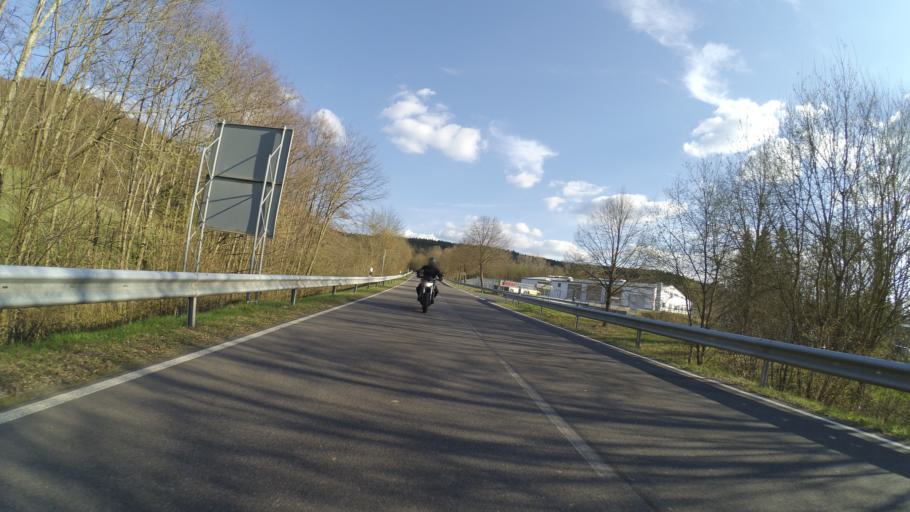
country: DE
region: Rheinland-Pfalz
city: Mullenbach
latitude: 50.3195
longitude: 6.9208
